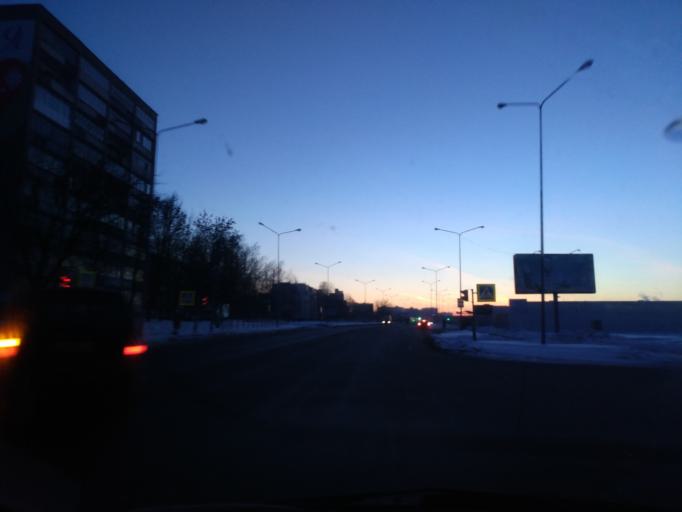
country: BY
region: Mogilev
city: Mahilyow
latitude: 53.8810
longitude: 30.3216
